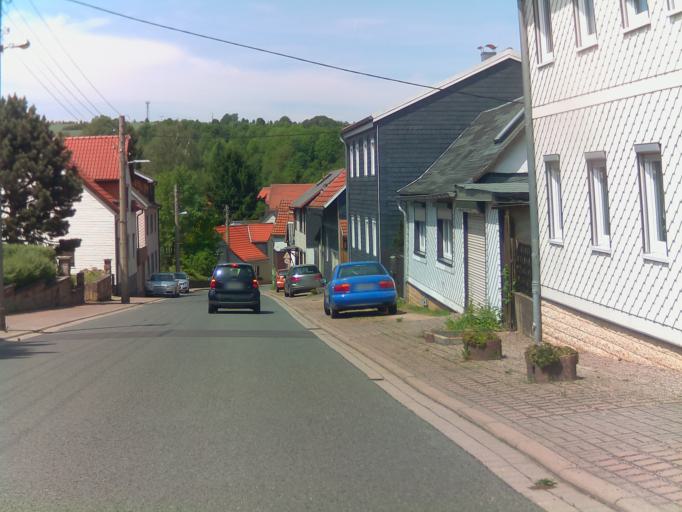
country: DE
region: Thuringia
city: Geraberg
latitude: 50.7183
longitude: 10.8511
